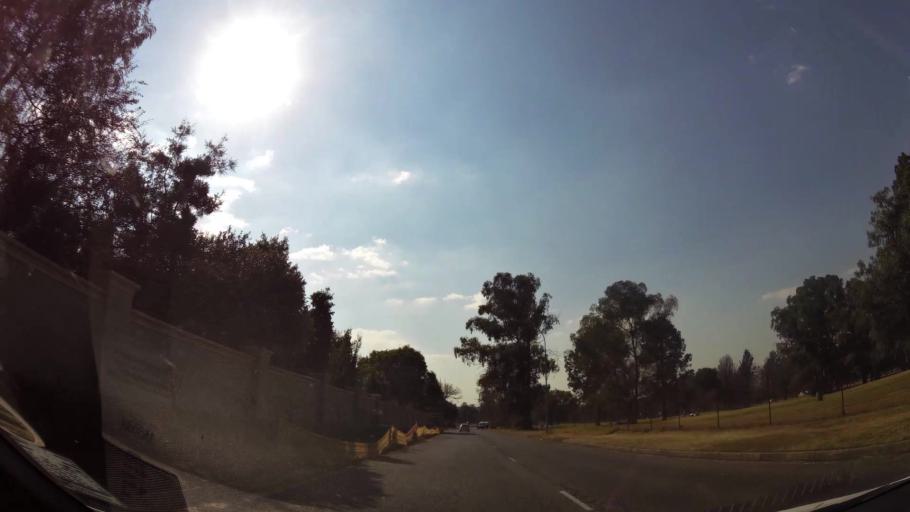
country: ZA
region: Gauteng
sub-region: Ekurhuleni Metropolitan Municipality
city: Benoni
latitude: -26.1835
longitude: 28.2925
